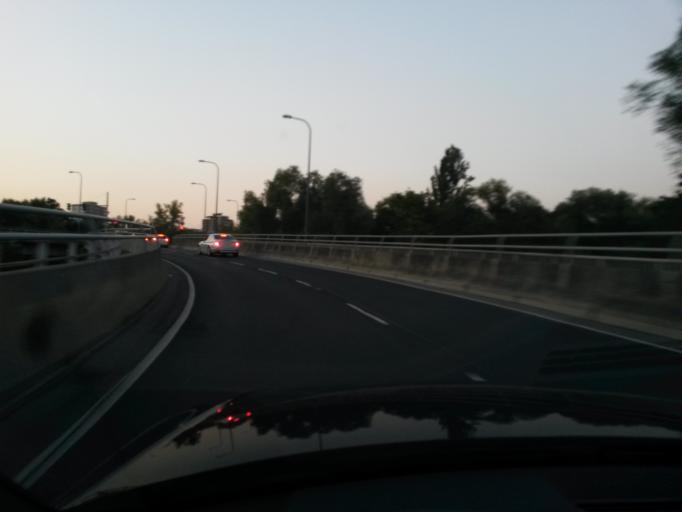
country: DE
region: Bavaria
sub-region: Regierungsbezirk Unterfranken
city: Wuerzburg
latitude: 49.7694
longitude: 9.9393
